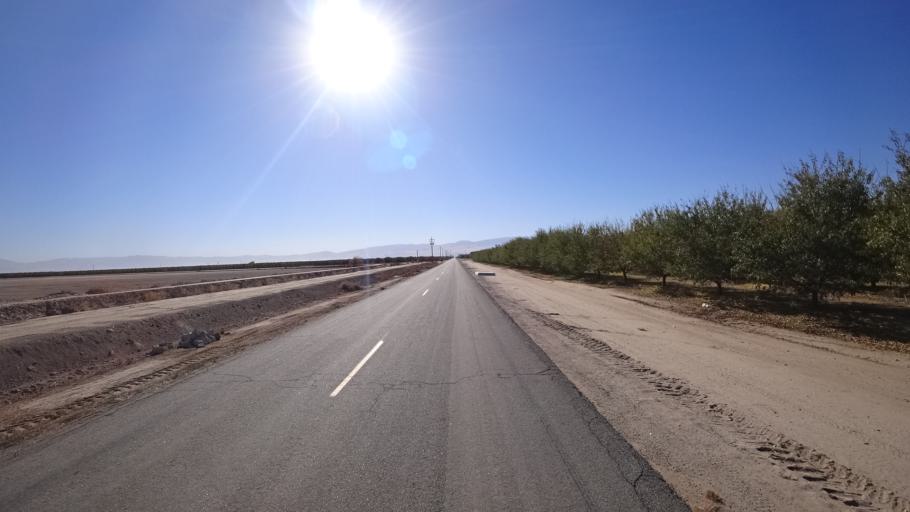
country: US
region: California
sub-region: Kern County
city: Greenfield
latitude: 35.2575
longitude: -119.0567
